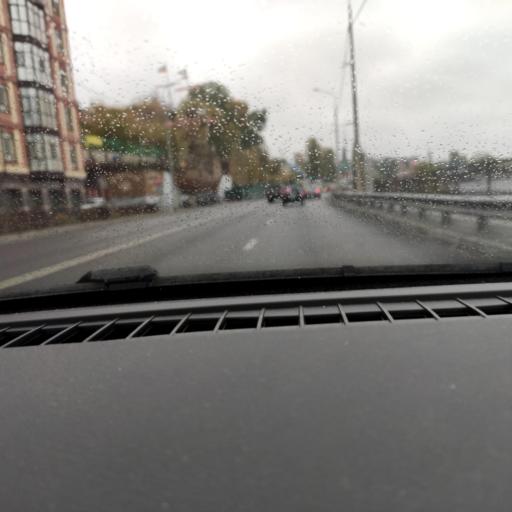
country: RU
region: Voronezj
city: Voronezh
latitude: 51.6817
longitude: 39.2282
